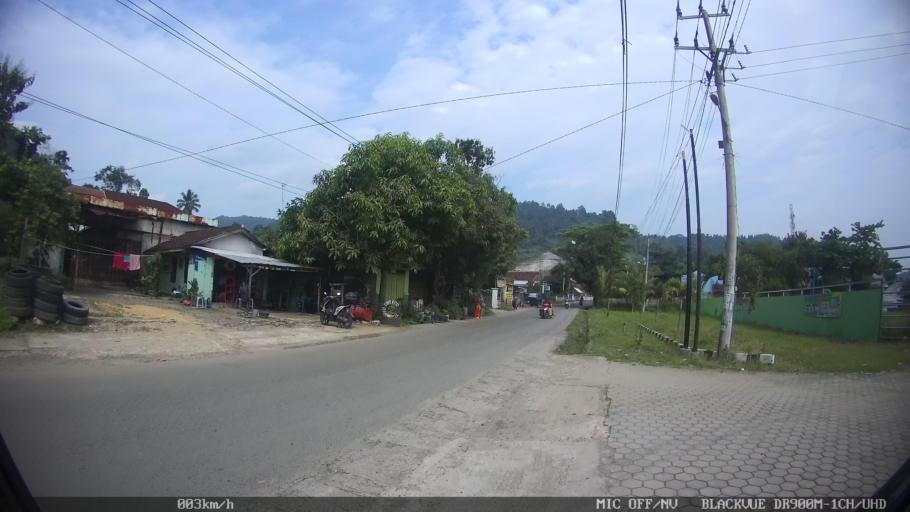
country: ID
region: Lampung
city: Bandarlampung
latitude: -5.4729
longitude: 105.2460
